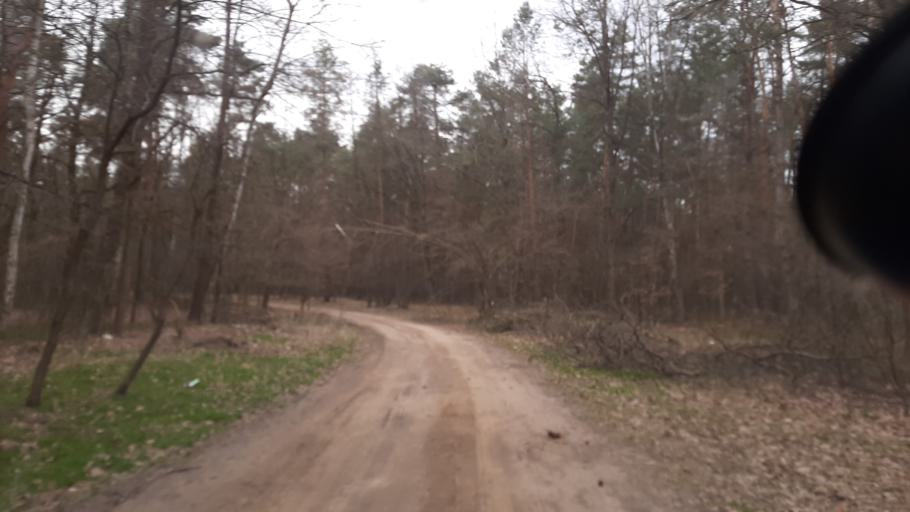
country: PL
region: Lublin Voivodeship
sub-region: Powiat lubartowski
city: Abramow
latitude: 51.4429
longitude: 22.3447
